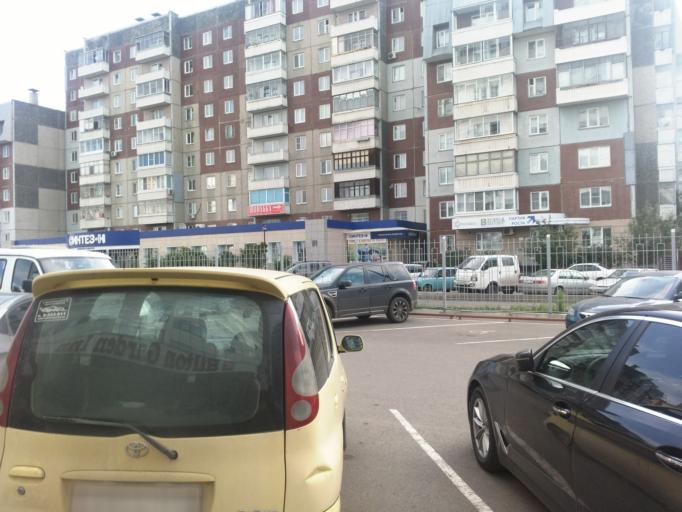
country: RU
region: Krasnoyarskiy
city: Krasnoyarsk
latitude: 56.0359
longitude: 92.8980
